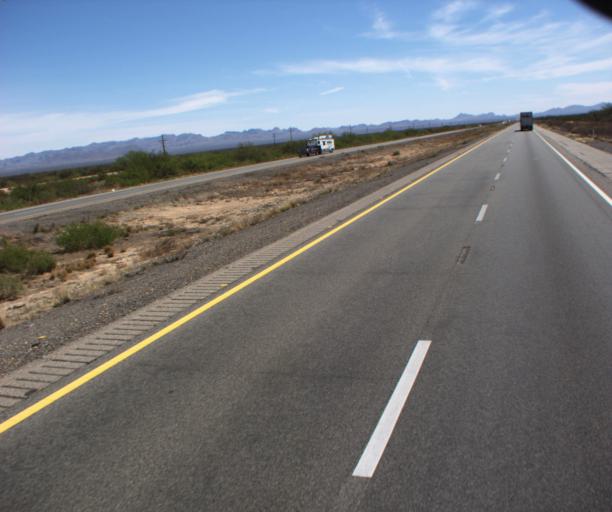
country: US
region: Arizona
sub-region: Cochise County
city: Willcox
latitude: 32.2915
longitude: -109.3294
